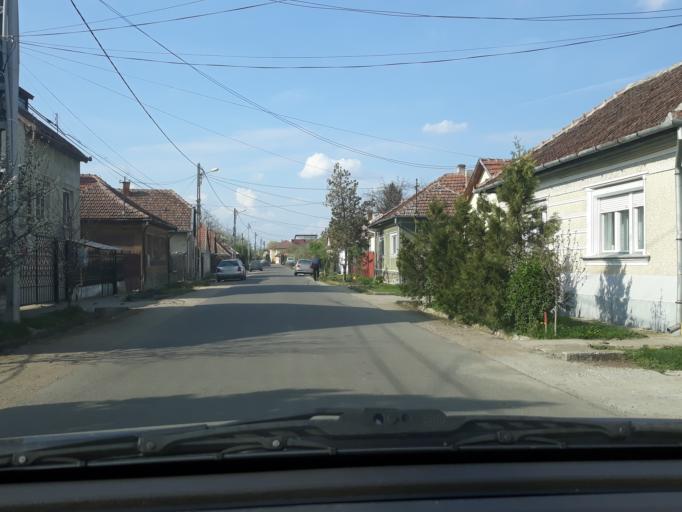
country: RO
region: Bihor
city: Margita
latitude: 47.3461
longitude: 22.3292
